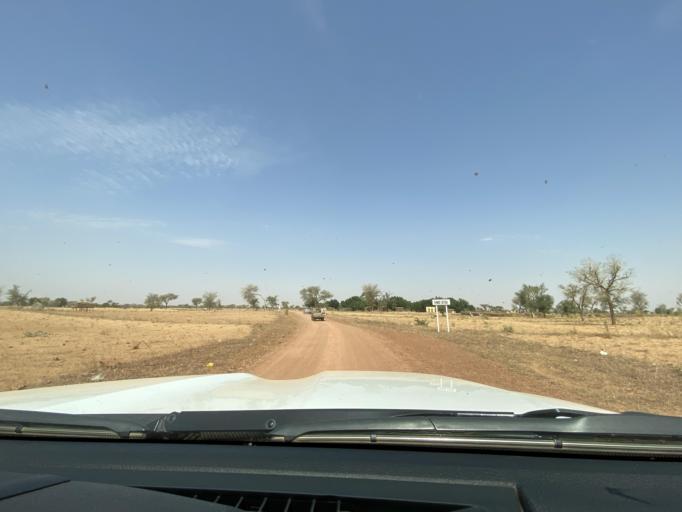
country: NE
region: Dosso
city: Birnin Gaoure
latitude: 13.2408
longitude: 2.8667
